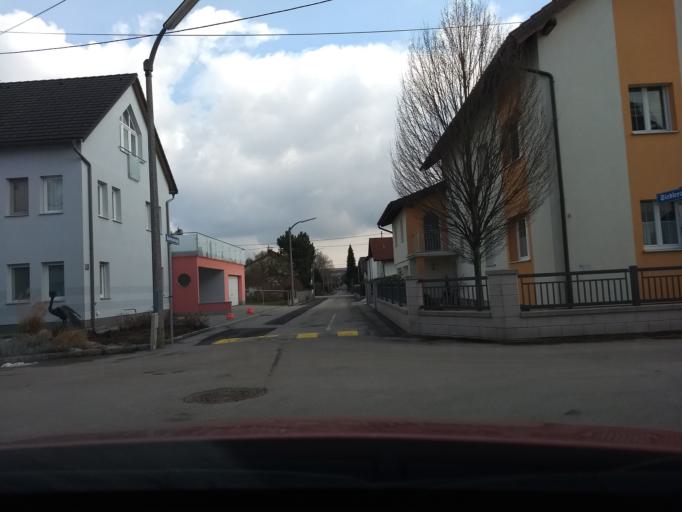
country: AT
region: Upper Austria
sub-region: Politischer Bezirk Steyr-Land
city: Garsten
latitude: 48.0448
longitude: 14.3845
